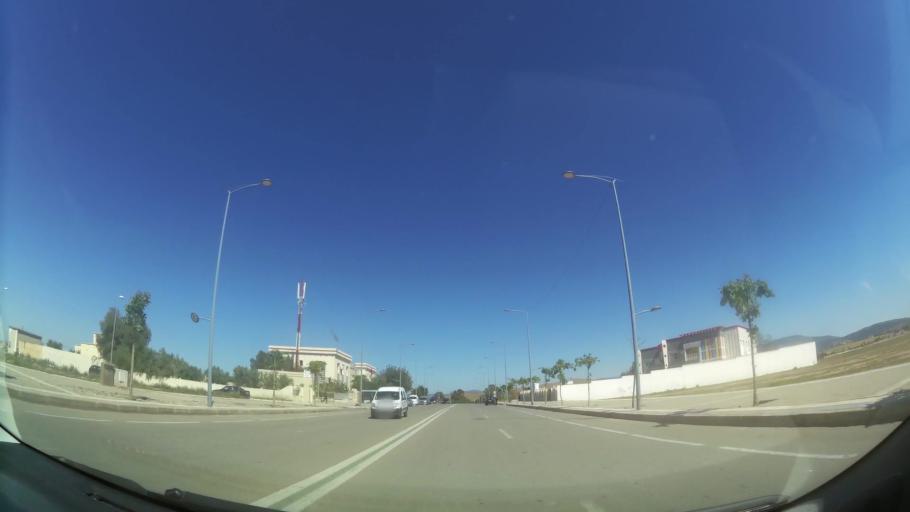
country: MA
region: Oriental
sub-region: Oujda-Angad
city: Oujda
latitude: 34.6669
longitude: -1.8684
